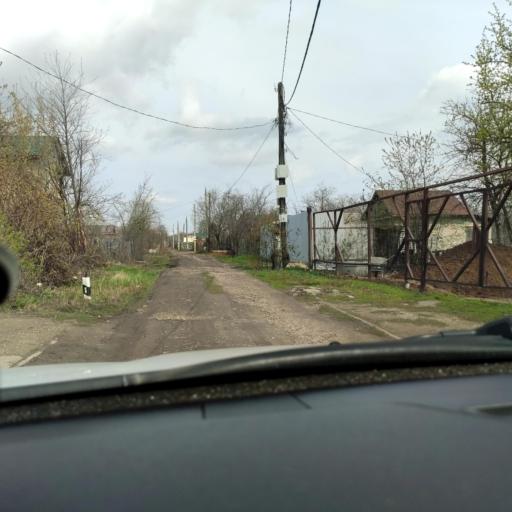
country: RU
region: Samara
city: Petra-Dubrava
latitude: 53.2749
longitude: 50.2988
